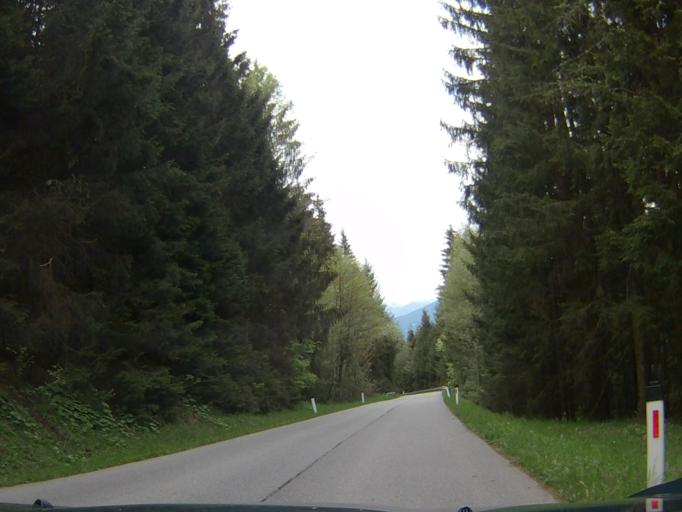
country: AT
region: Carinthia
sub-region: Politischer Bezirk Villach Land
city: Stockenboi
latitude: 46.7370
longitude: 13.5642
